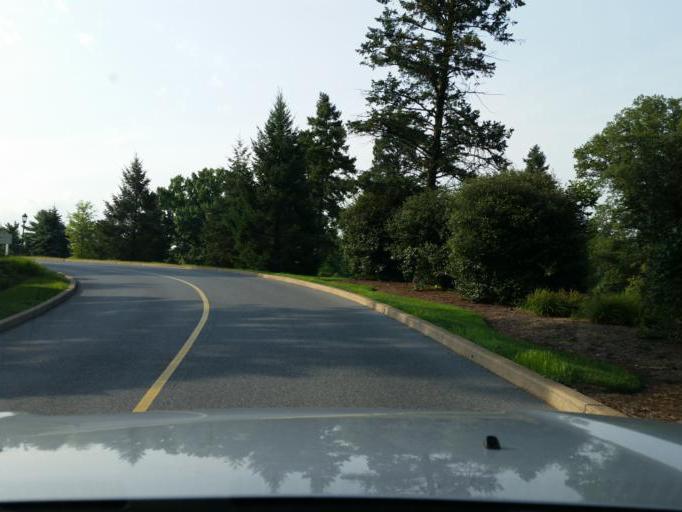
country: US
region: Pennsylvania
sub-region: Dauphin County
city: Hershey
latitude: 40.2999
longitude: -76.6574
